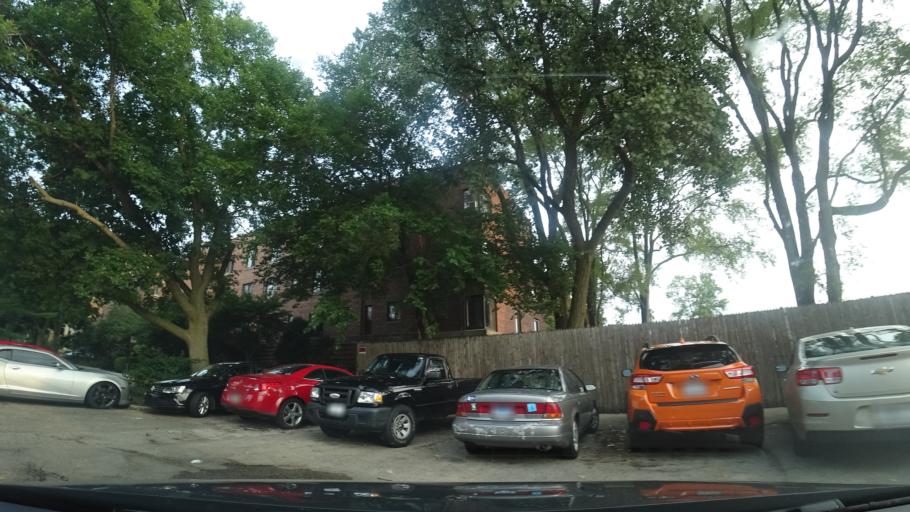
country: US
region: Illinois
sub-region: Cook County
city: Evanston
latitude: 42.0140
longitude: -87.6621
